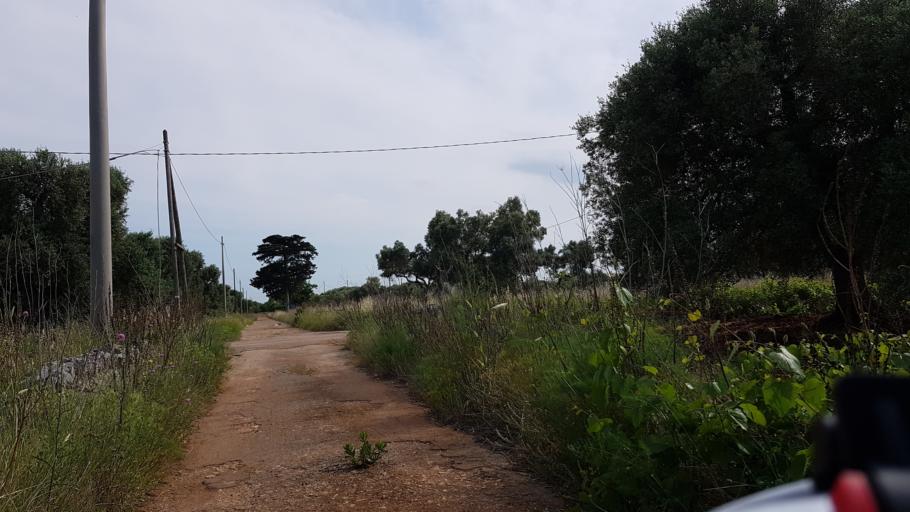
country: IT
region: Apulia
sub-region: Provincia di Brindisi
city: San Vito dei Normanni
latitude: 40.6486
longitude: 17.7708
